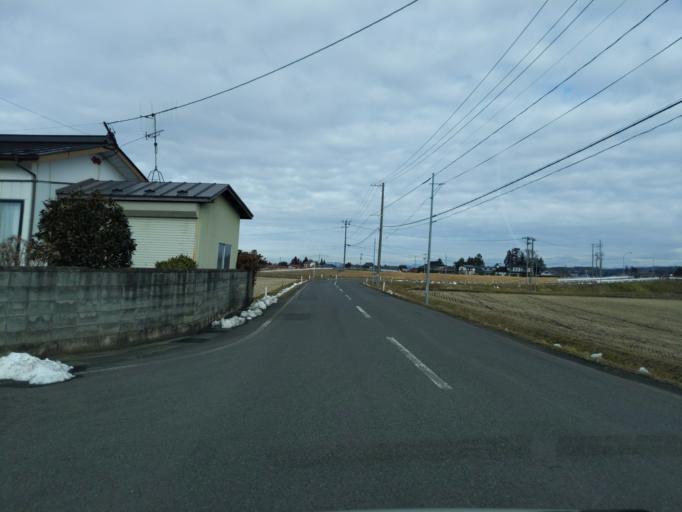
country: JP
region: Iwate
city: Mizusawa
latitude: 39.0806
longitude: 141.1653
